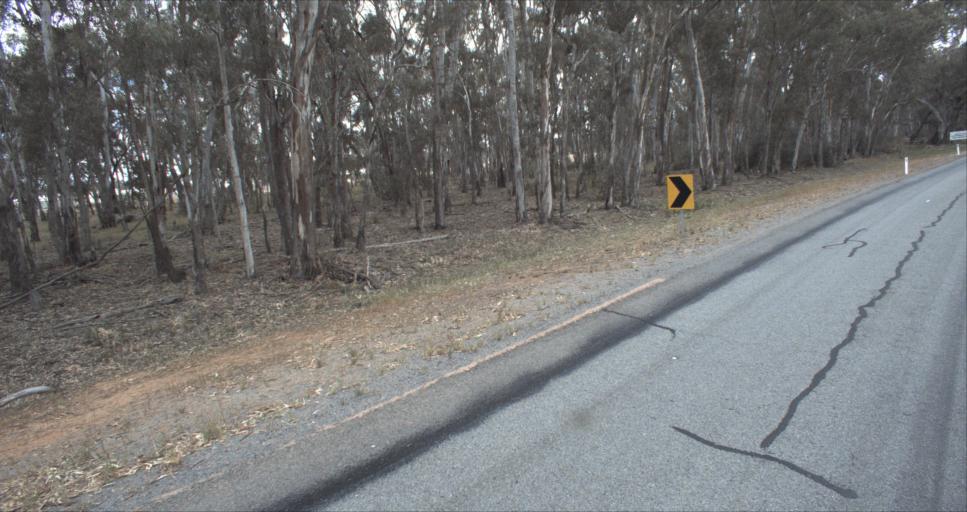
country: AU
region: New South Wales
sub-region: Leeton
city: Leeton
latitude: -34.6339
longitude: 146.3757
